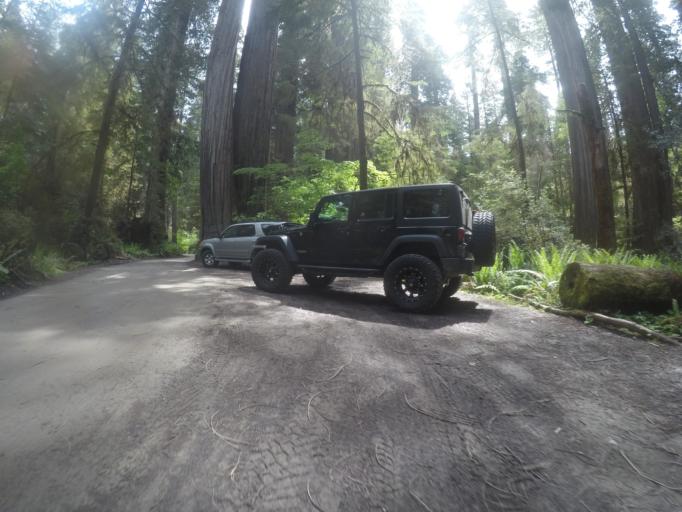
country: US
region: California
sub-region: Del Norte County
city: Bertsch-Oceanview
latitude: 41.7692
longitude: -124.1084
